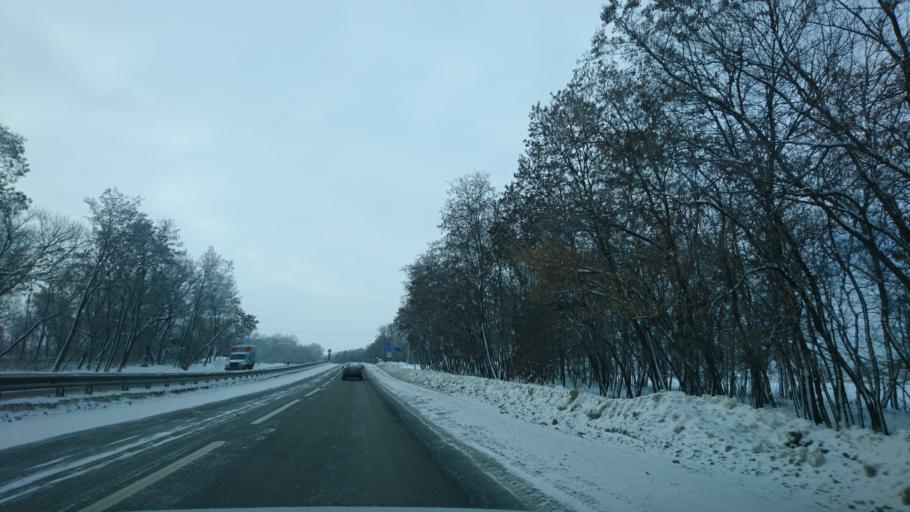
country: RU
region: Belgorod
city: Mayskiy
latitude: 50.4866
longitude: 36.4127
